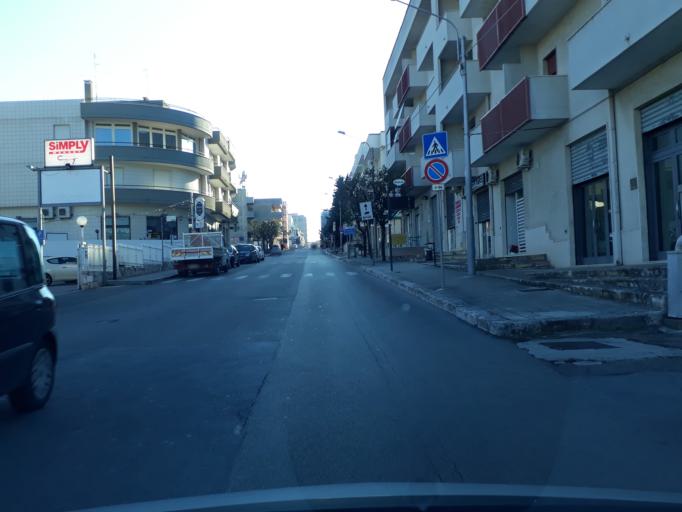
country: IT
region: Apulia
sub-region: Provincia di Bari
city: Locorotondo
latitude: 40.7603
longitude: 17.3291
